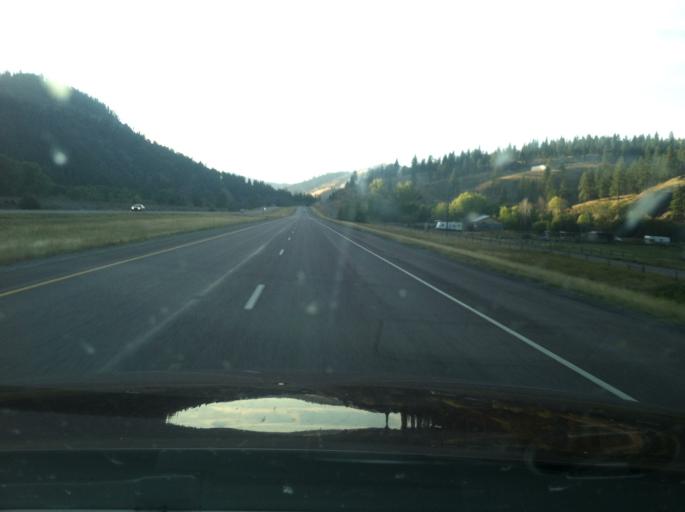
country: US
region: Montana
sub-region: Missoula County
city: Clinton
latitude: 46.7006
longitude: -113.4943
